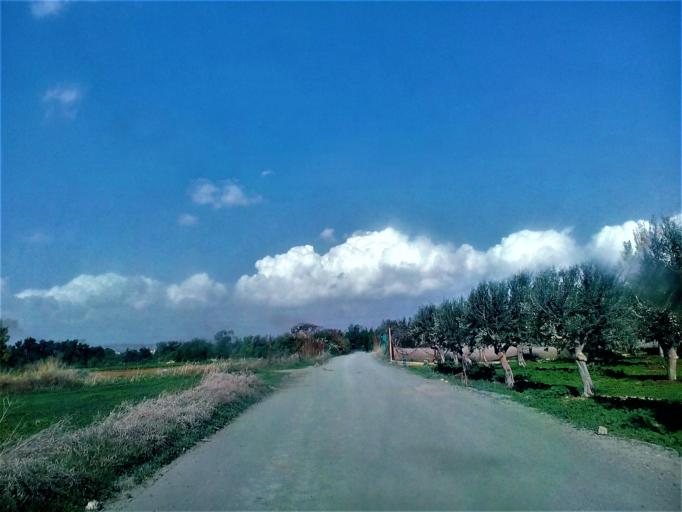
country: CY
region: Limassol
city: Ypsonas
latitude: 34.6643
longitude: 32.9681
